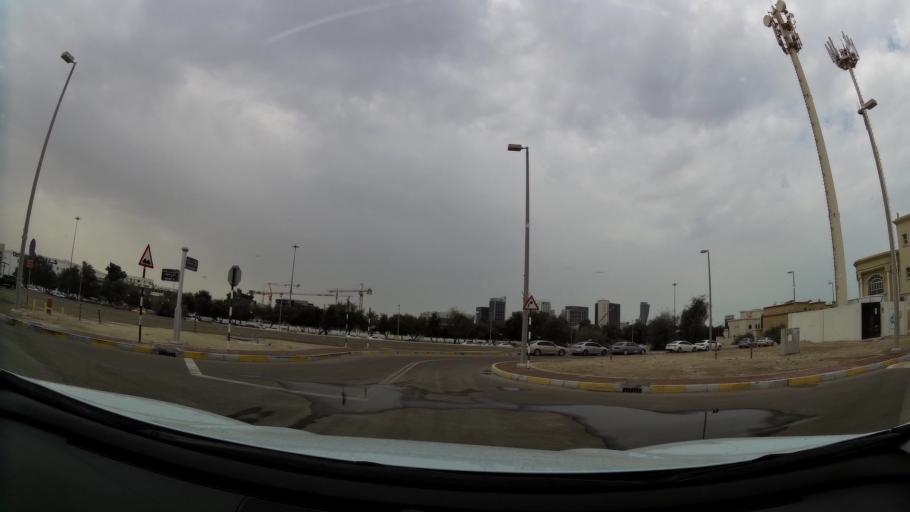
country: AE
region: Abu Dhabi
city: Abu Dhabi
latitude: 24.4267
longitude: 54.4512
